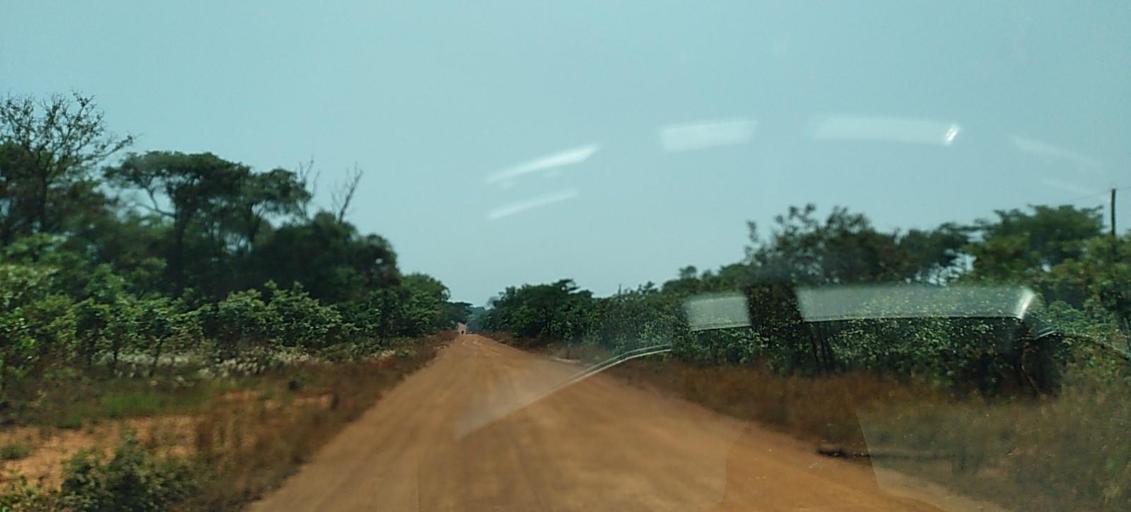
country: ZM
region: North-Western
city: Kansanshi
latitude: -11.9876
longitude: 26.8472
